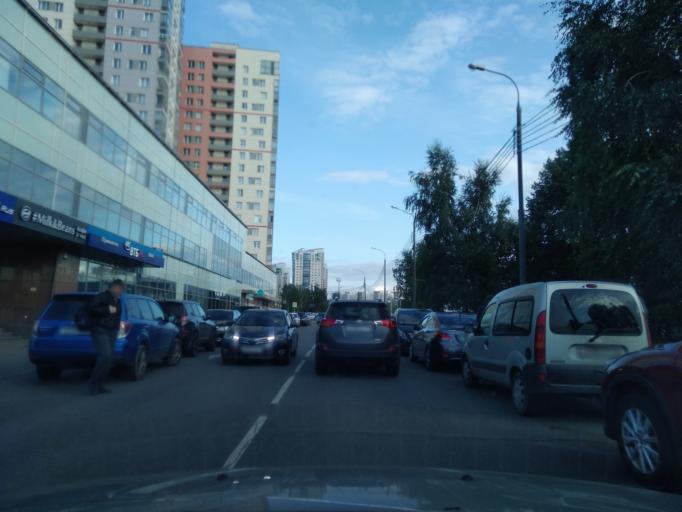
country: RU
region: Moscow
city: Nikulino
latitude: 55.6795
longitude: 37.4680
